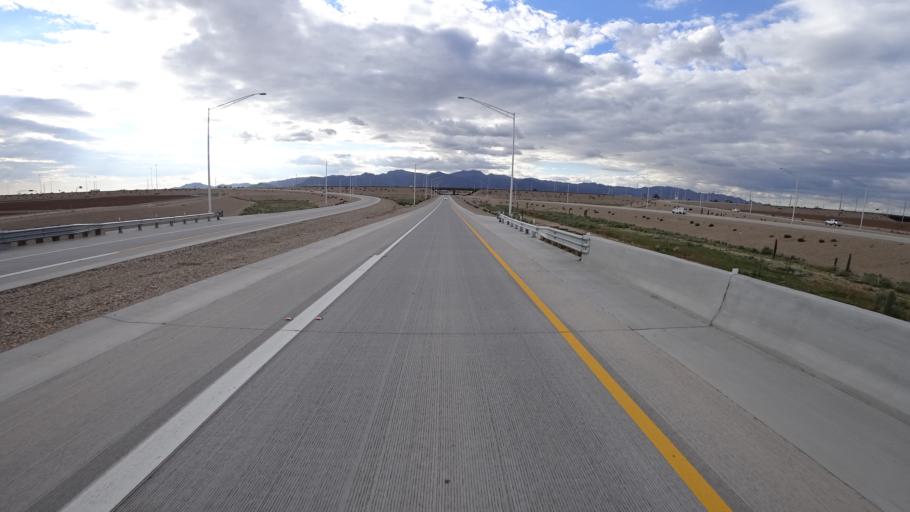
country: US
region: Arizona
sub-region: Maricopa County
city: Citrus Park
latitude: 33.5589
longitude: -112.4133
